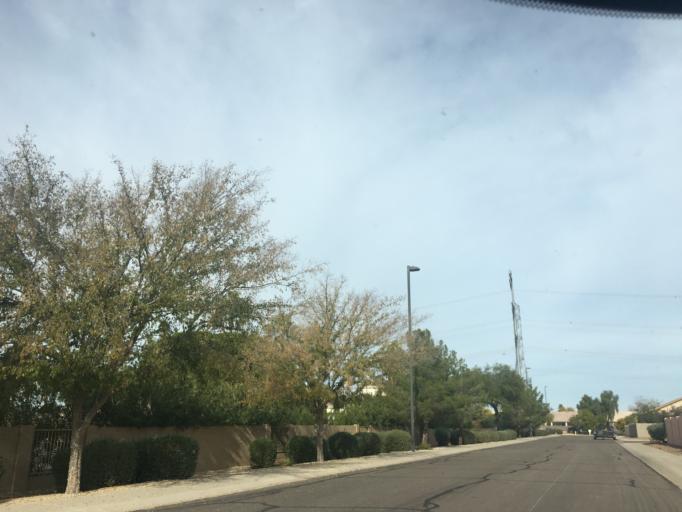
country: US
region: Arizona
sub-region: Maricopa County
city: Gilbert
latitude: 33.3552
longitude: -111.8095
